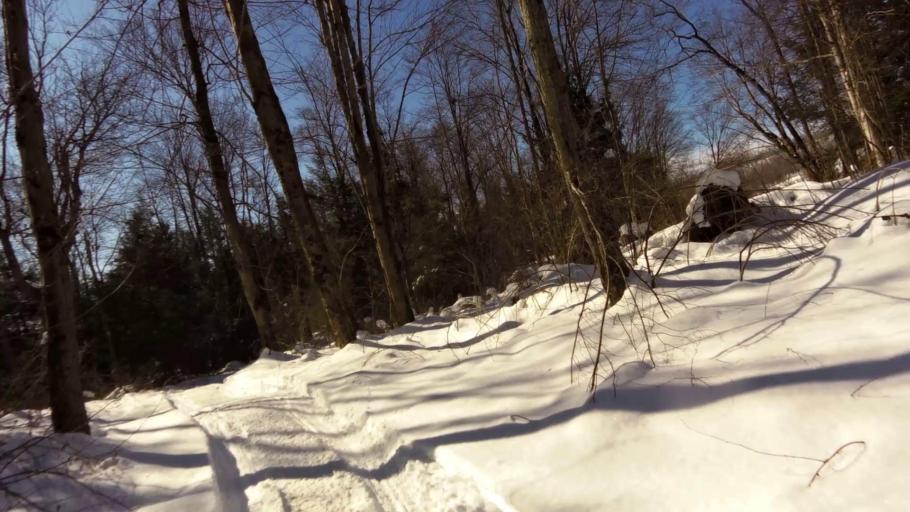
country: US
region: New York
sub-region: Allegany County
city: Cuba
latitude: 42.3491
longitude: -78.3064
